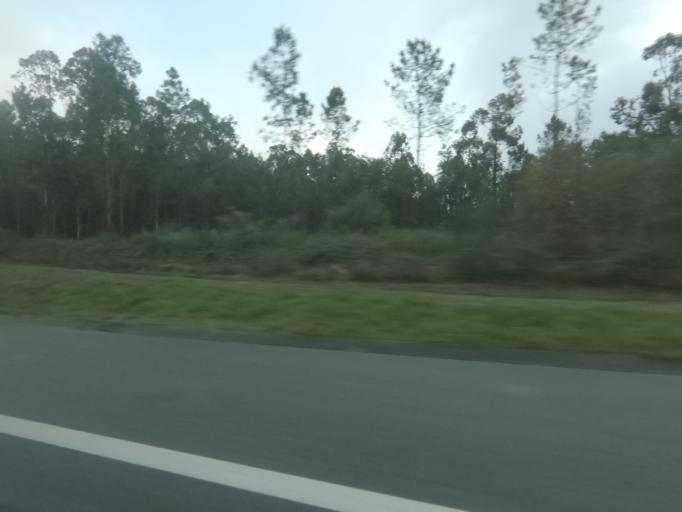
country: PT
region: Braga
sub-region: Barcelos
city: Galegos
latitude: 41.6255
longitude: -8.5583
